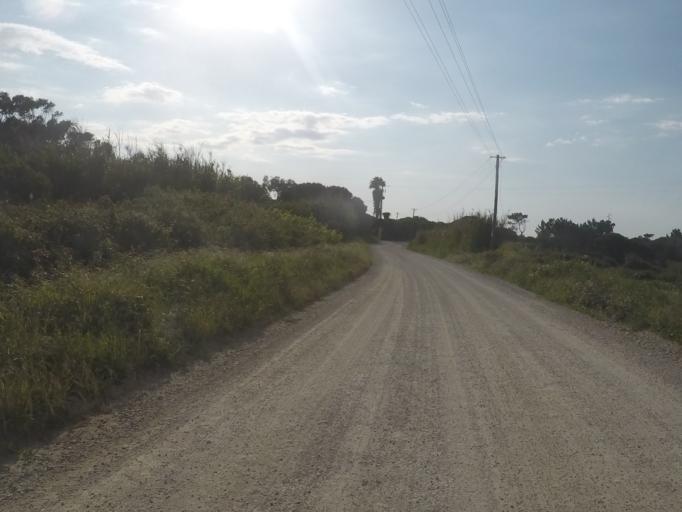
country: PT
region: Setubal
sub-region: Sesimbra
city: Sesimbra
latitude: 38.4406
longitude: -9.1928
